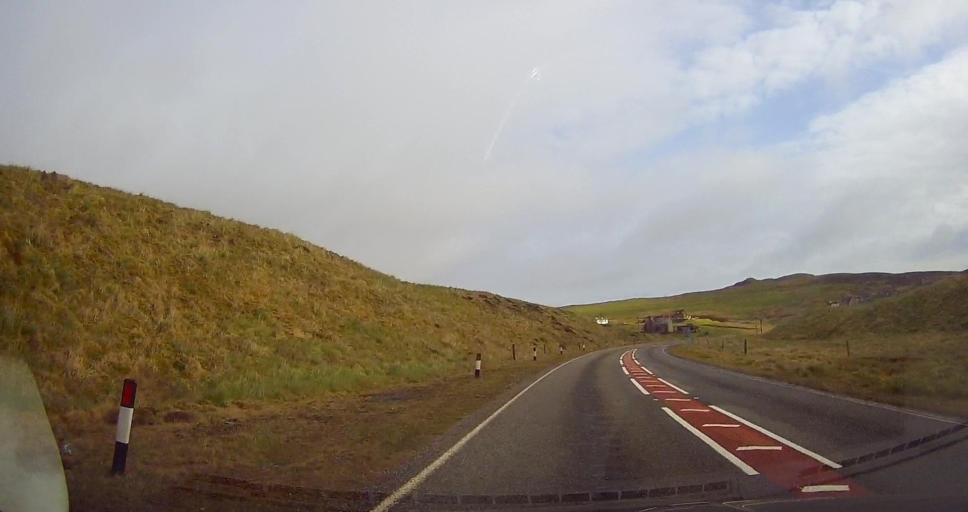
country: GB
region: Scotland
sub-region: Shetland Islands
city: Lerwick
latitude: 60.1015
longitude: -1.2341
